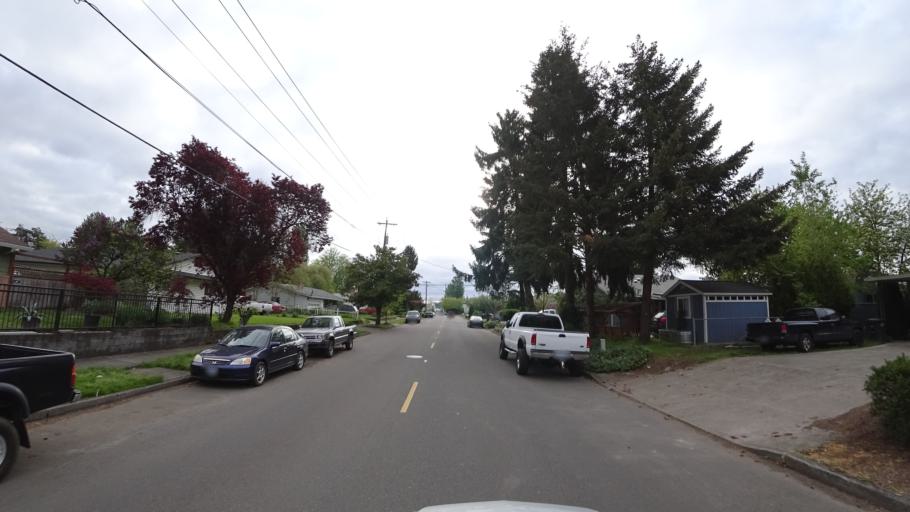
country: US
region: Oregon
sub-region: Washington County
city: Hillsboro
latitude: 45.5366
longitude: -122.9592
